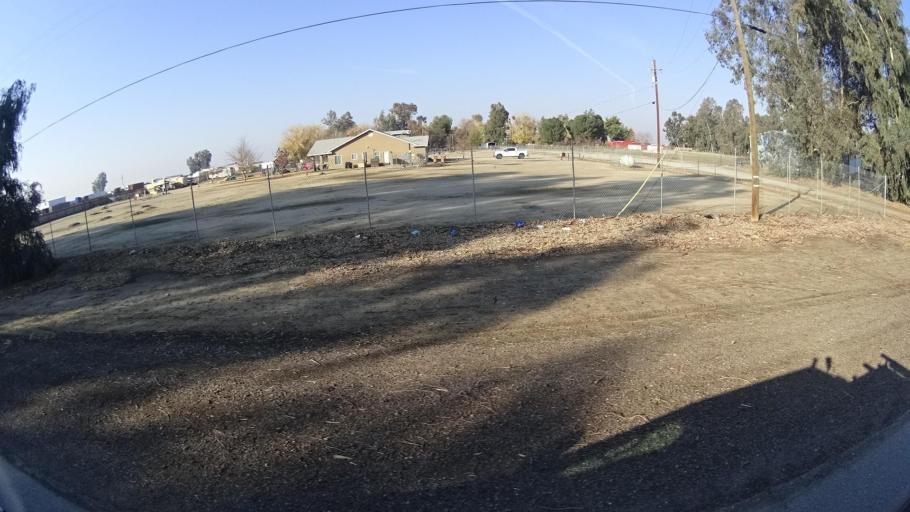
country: US
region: California
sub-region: Kern County
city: Greenfield
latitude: 35.1946
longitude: -119.0033
